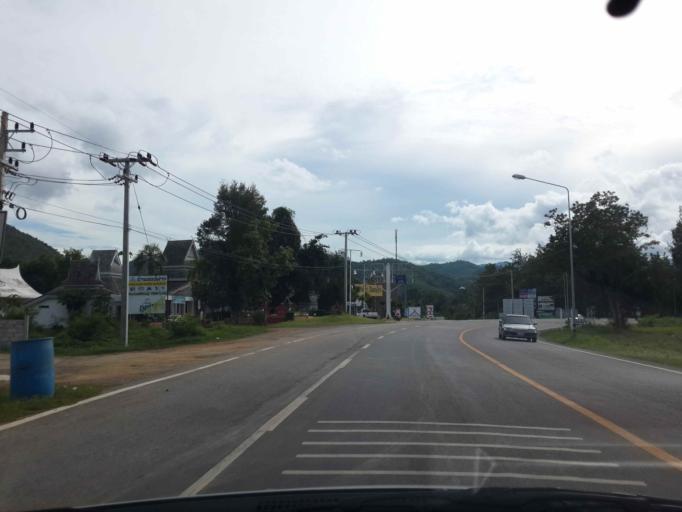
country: TH
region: Ratchaburi
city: Suan Phueng
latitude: 13.5425
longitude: 99.3051
